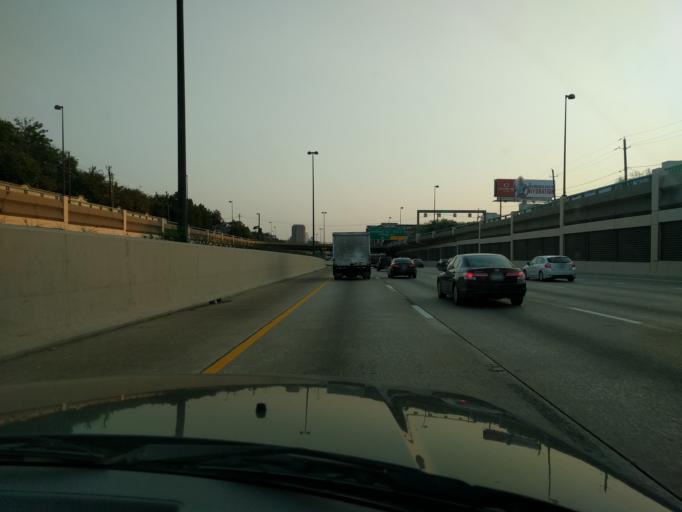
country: US
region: Texas
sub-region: Dallas County
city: Highland Park
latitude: 32.8282
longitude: -96.7830
